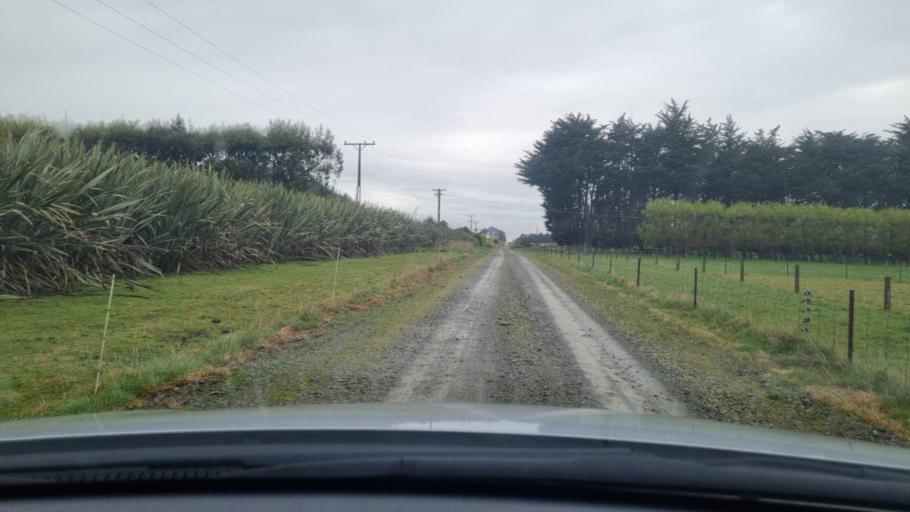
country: NZ
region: Southland
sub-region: Invercargill City
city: Invercargill
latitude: -46.3222
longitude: 168.3299
